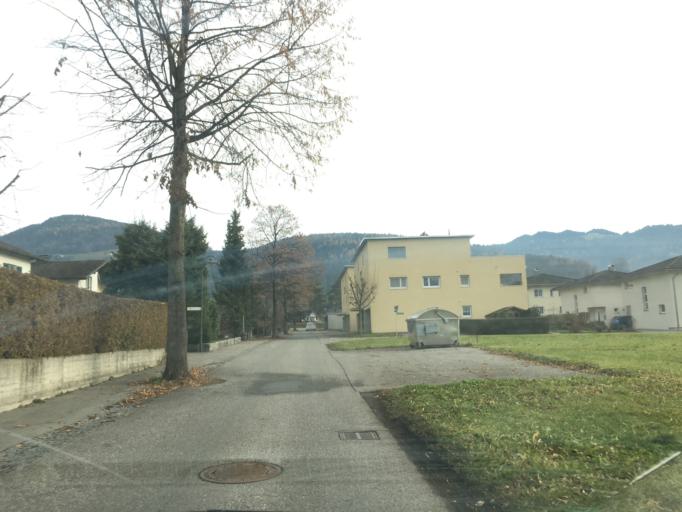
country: AT
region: Vorarlberg
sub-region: Politischer Bezirk Feldkirch
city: Weiler
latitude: 47.3017
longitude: 9.6444
